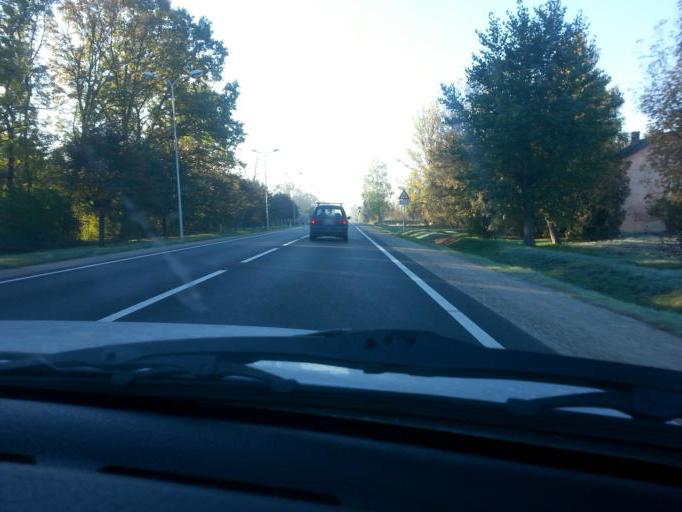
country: LT
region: Siauliu apskritis
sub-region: Joniskis
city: Joniskis
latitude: 56.4128
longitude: 23.6829
